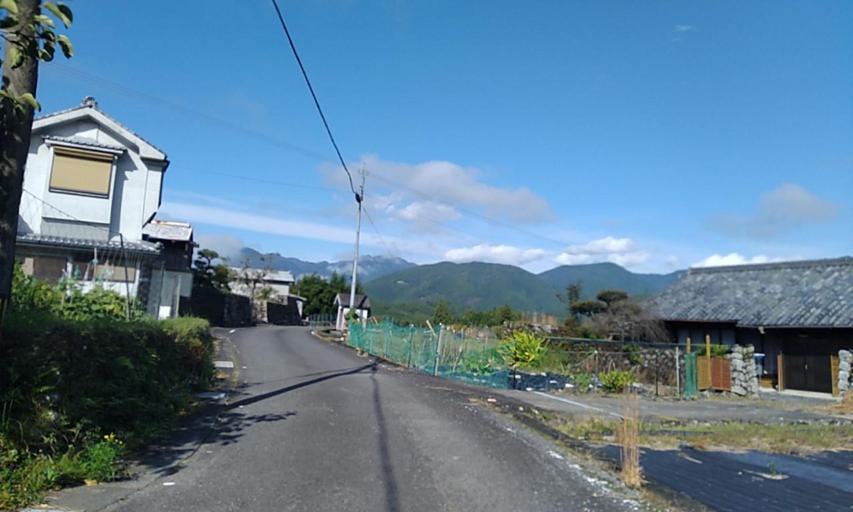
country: JP
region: Wakayama
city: Shingu
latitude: 33.9192
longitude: 135.9871
